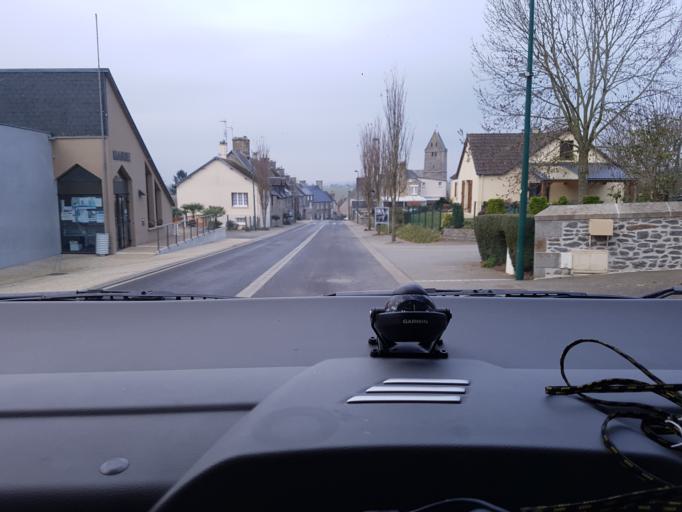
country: FR
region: Lower Normandy
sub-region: Departement de la Manche
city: Brecey
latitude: 48.7515
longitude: -1.1208
